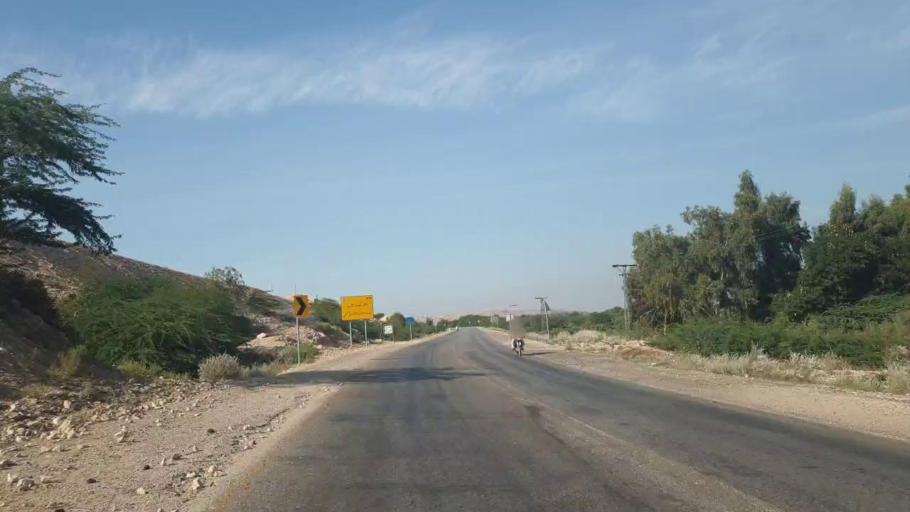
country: PK
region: Sindh
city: Sehwan
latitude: 26.3240
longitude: 67.8839
